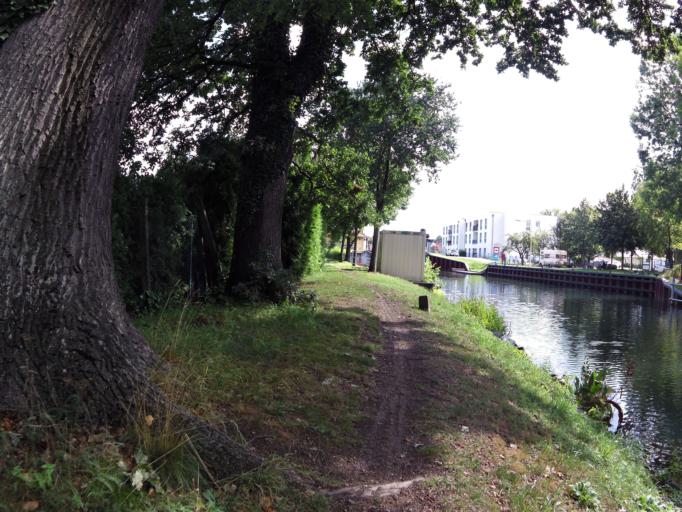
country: DE
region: Brandenburg
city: Storkow
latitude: 52.2584
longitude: 13.9305
